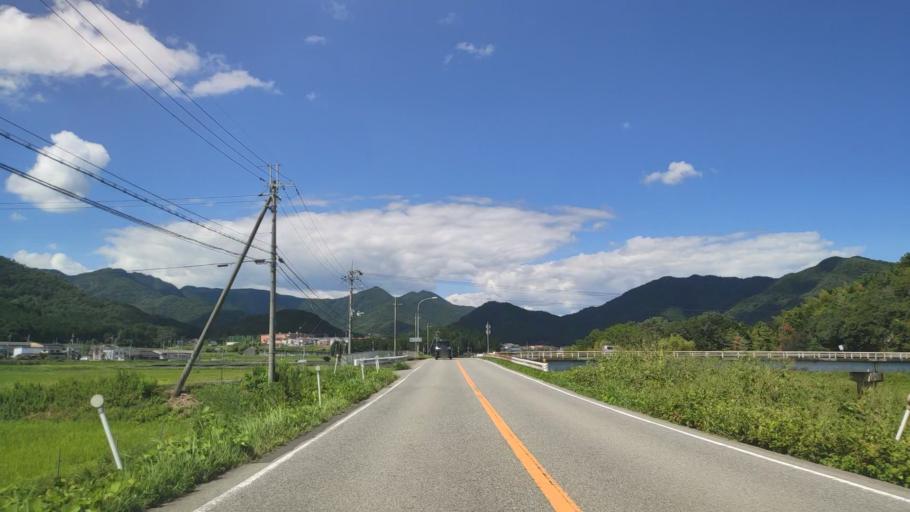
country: JP
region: Kyoto
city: Fukuchiyama
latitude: 35.1886
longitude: 135.1226
